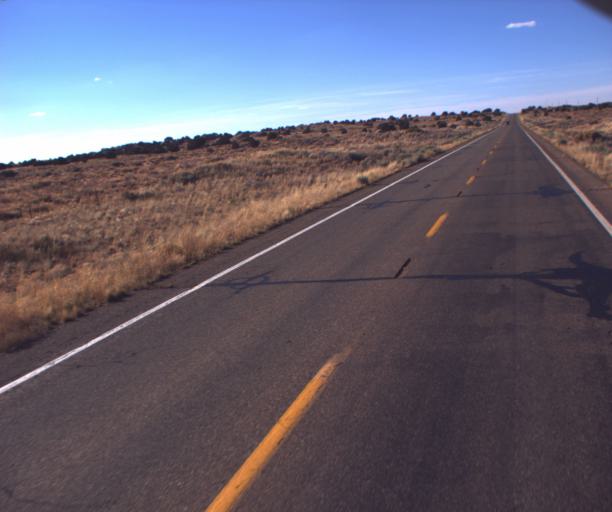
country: US
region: Arizona
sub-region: Coconino County
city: Kaibito
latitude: 36.5888
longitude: -111.1547
